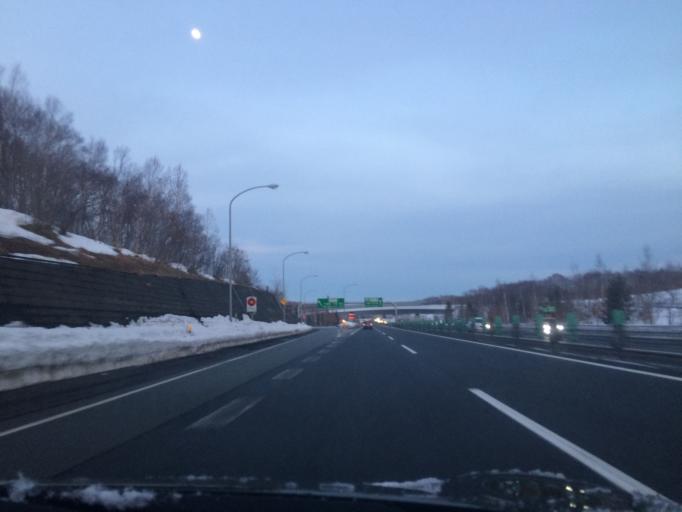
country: JP
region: Hokkaido
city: Chitose
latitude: 42.8467
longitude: 141.5809
